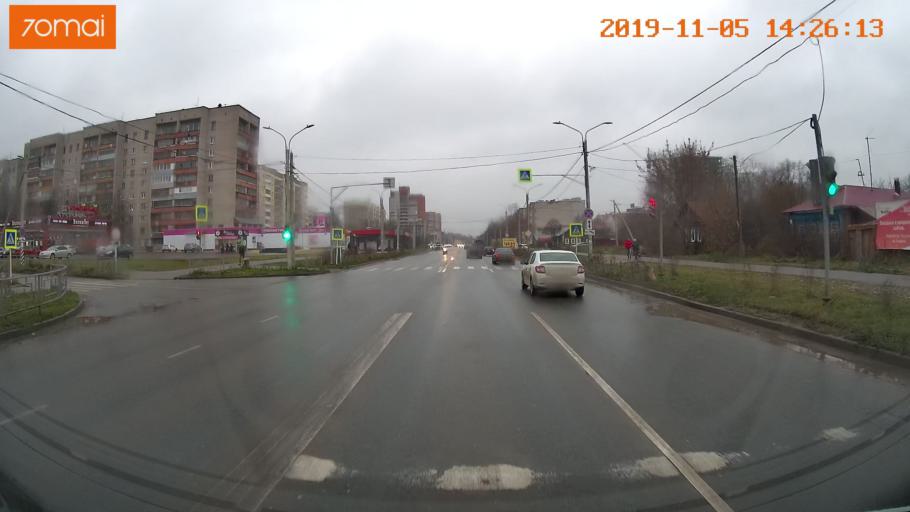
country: RU
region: Ivanovo
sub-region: Gorod Ivanovo
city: Ivanovo
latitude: 56.9713
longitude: 40.9858
